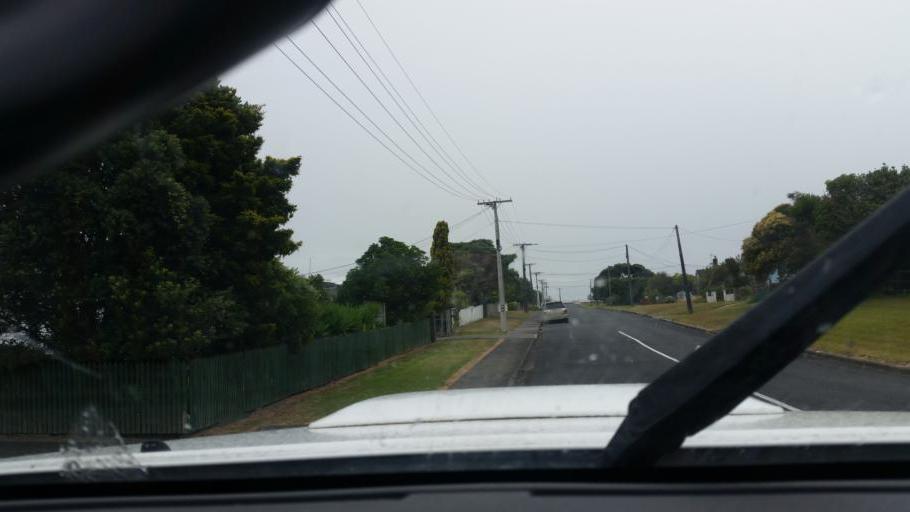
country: NZ
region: Northland
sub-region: Kaipara District
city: Dargaville
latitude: -35.9354
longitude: 173.8699
